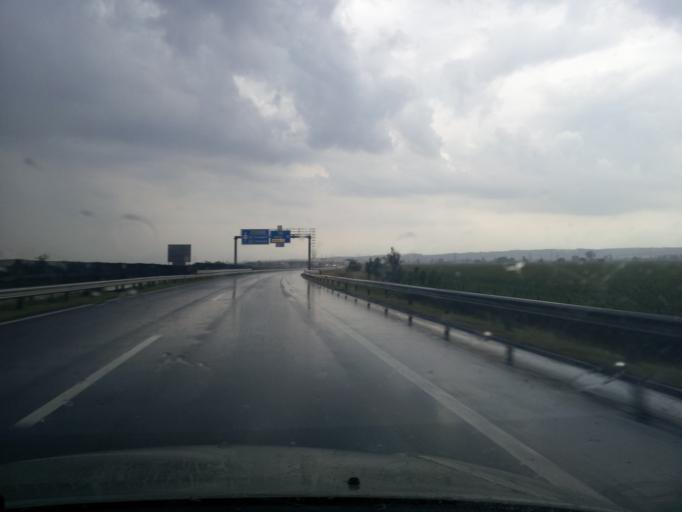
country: HU
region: Borsod-Abauj-Zemplen
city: Alsozsolca
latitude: 48.0704
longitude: 20.8487
